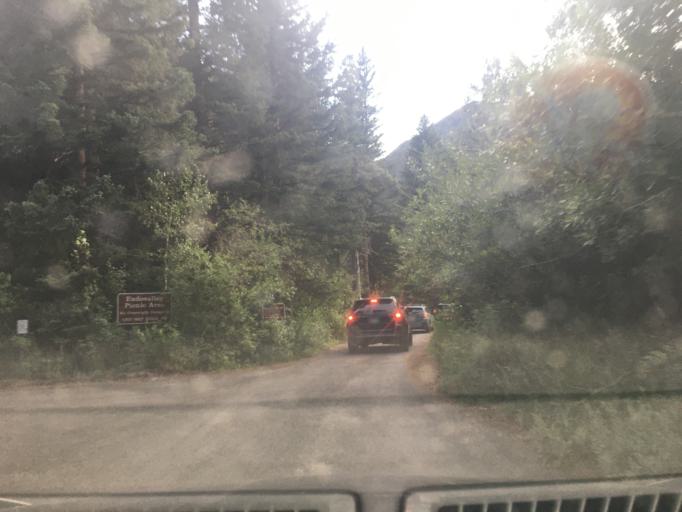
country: US
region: Colorado
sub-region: Larimer County
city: Estes Park
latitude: 40.4142
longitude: -105.6563
